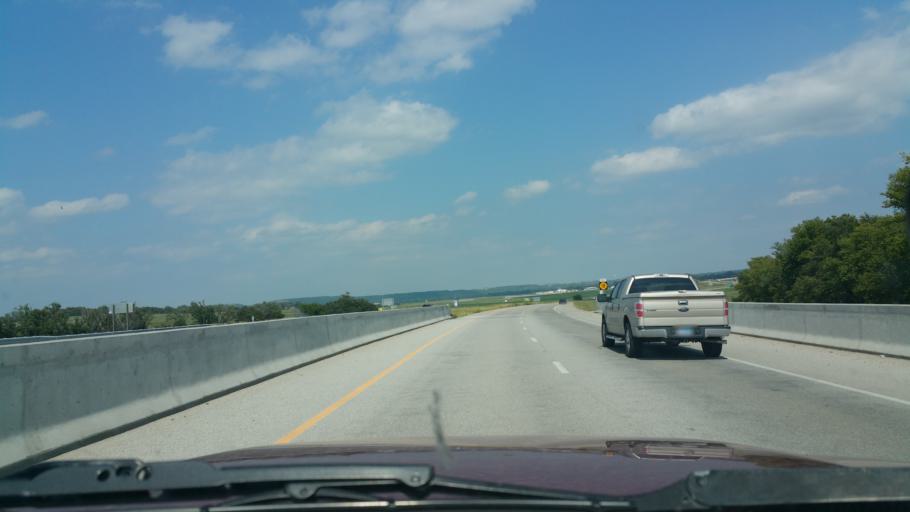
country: US
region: Kansas
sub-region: Riley County
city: Ogden
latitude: 39.1217
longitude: -96.6887
